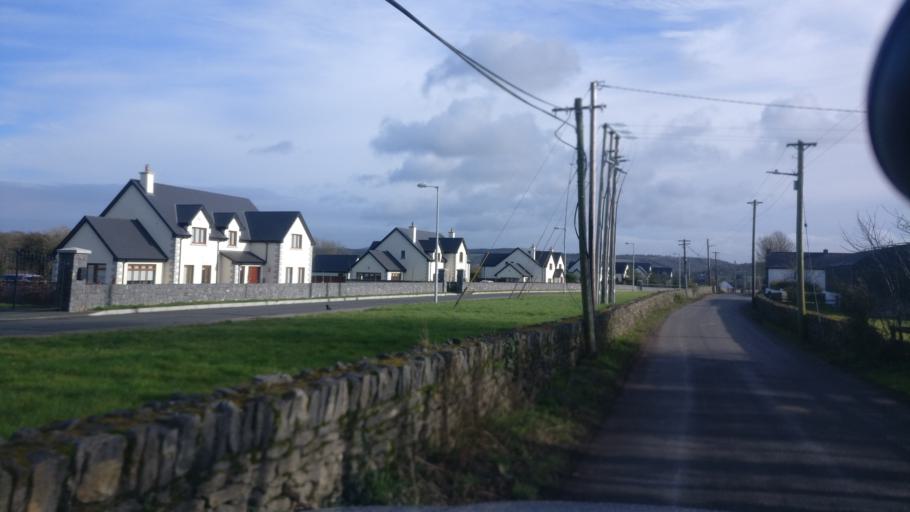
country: IE
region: Leinster
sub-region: Kilkenny
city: Thomastown
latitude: 52.5252
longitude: -7.1605
